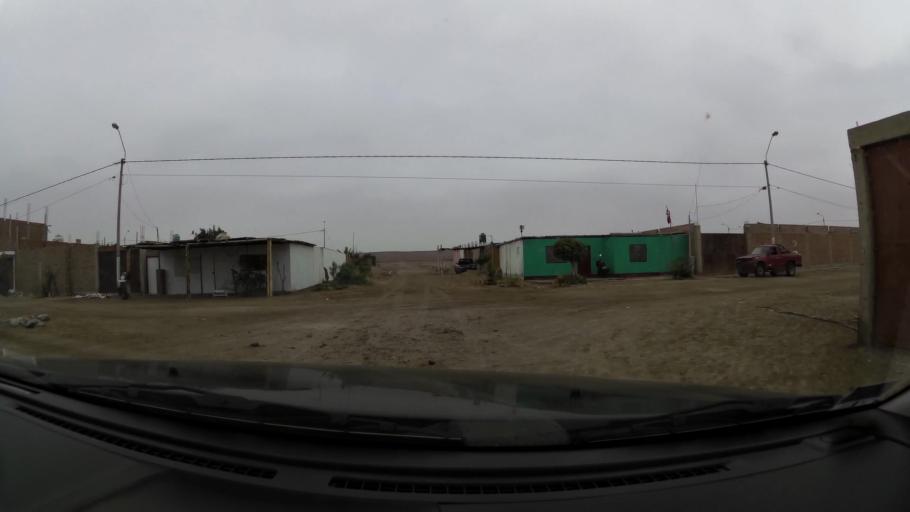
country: PE
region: Ica
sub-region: Provincia de Pisco
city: Paracas
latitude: -13.8347
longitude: -76.2467
